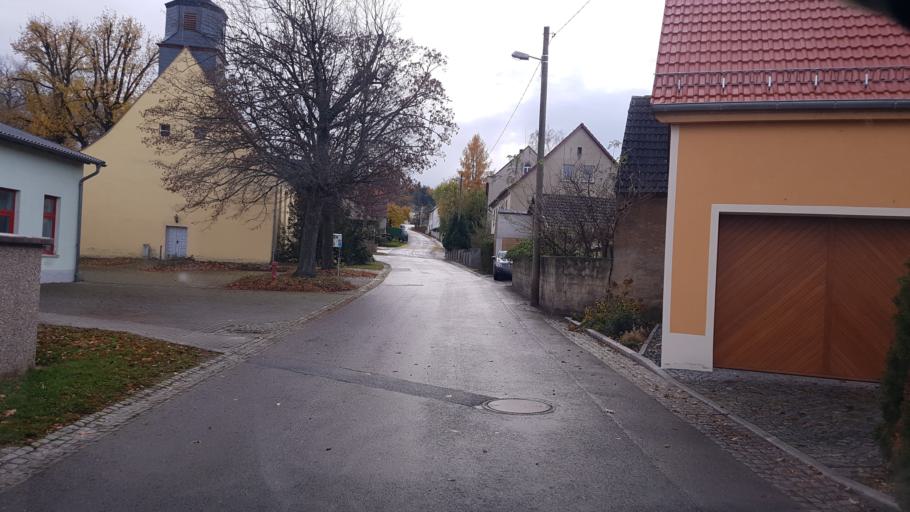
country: DE
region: Brandenburg
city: Grosskmehlen
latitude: 51.3430
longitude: 13.7335
